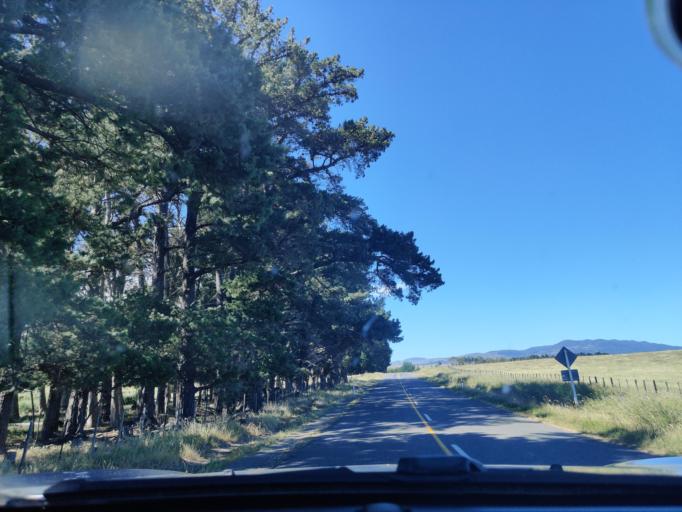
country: NZ
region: Wellington
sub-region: South Wairarapa District
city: Waipawa
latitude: -41.2037
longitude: 175.3653
